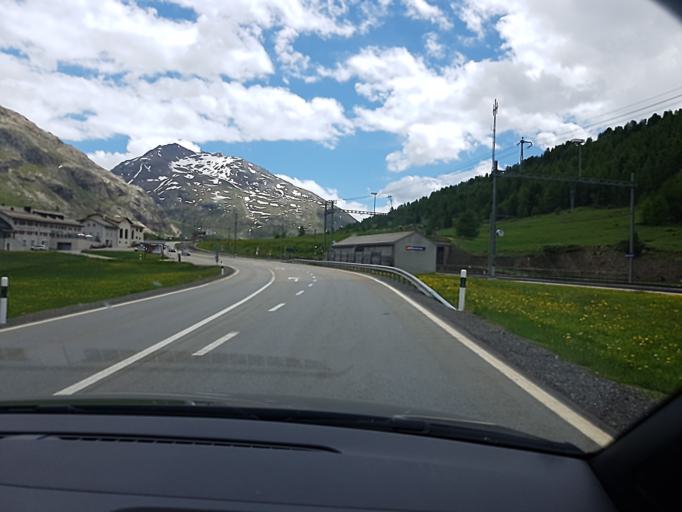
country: CH
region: Grisons
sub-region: Maloja District
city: Pontresina
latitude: 46.4456
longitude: 9.9685
